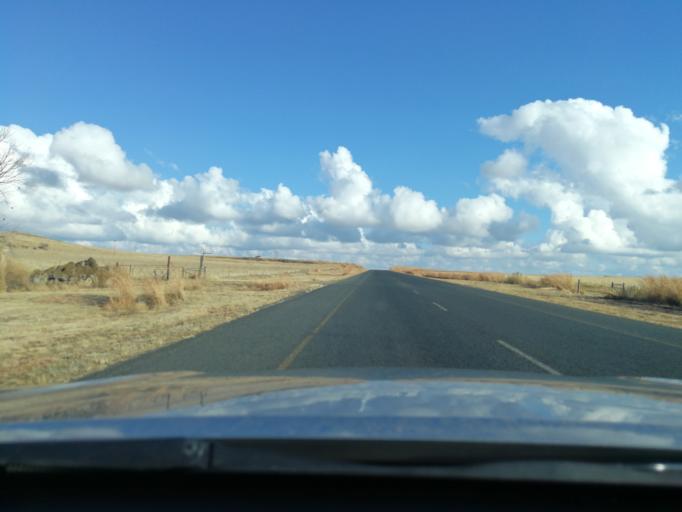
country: ZA
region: Orange Free State
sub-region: Thabo Mofutsanyana District Municipality
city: Bethlehem
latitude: -28.0805
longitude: 28.3574
